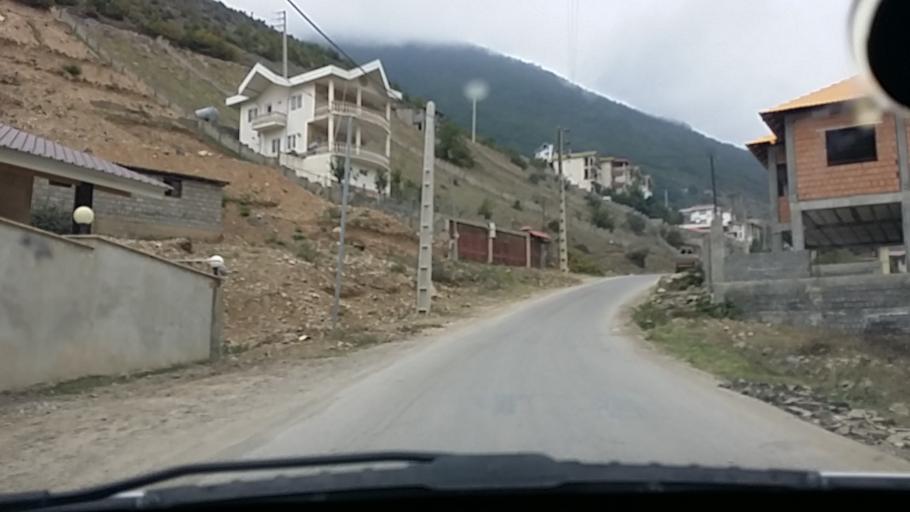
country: IR
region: Mazandaran
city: `Abbasabad
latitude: 36.4783
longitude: 51.1394
